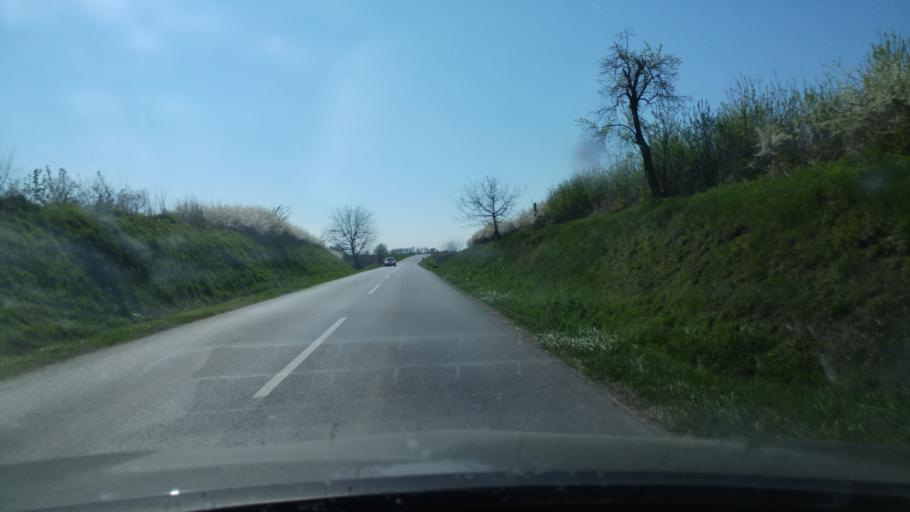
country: HR
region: Osjecko-Baranjska
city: Semeljci
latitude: 45.3535
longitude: 18.5160
